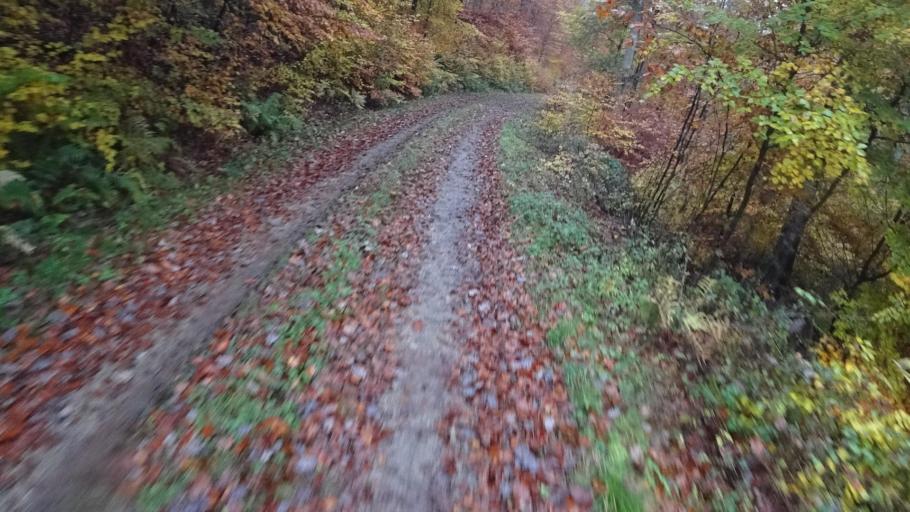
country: DE
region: Rheinland-Pfalz
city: Utzenhain
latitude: 50.1487
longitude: 7.6538
